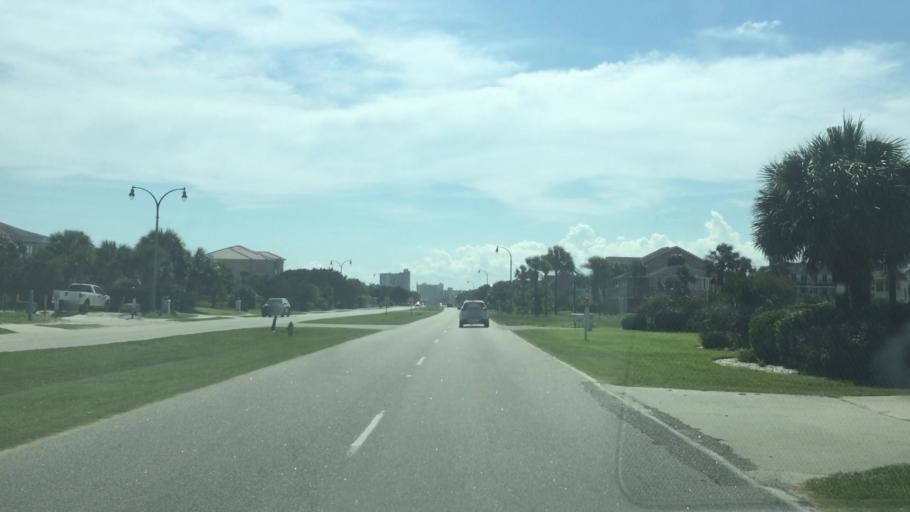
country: US
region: South Carolina
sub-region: Horry County
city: North Myrtle Beach
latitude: 33.8258
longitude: -78.6521
